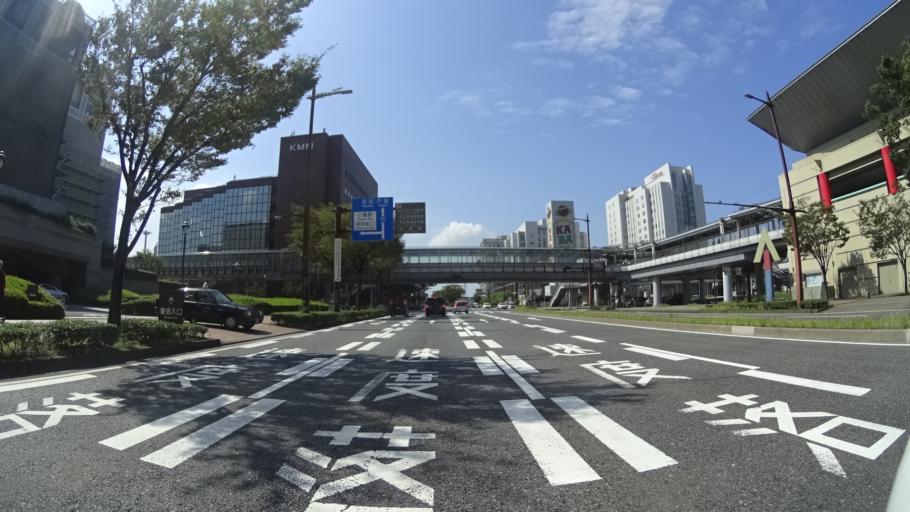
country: JP
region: Fukuoka
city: Kitakyushu
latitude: 33.8889
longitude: 130.8850
